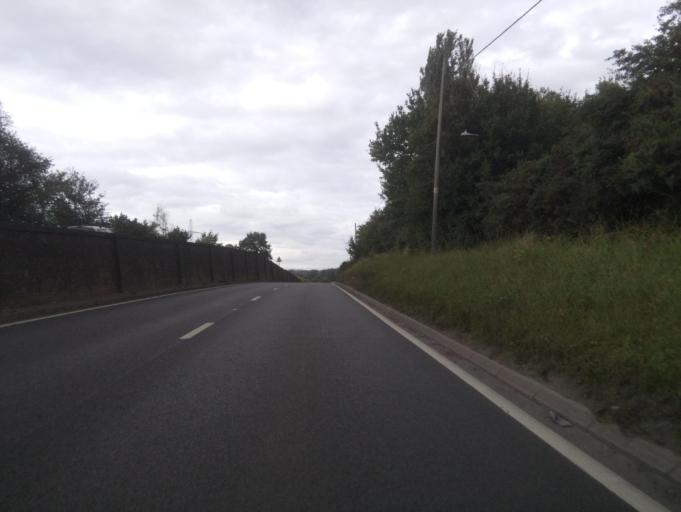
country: GB
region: England
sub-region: Warwickshire
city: Water Orton
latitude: 52.5118
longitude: -1.7171
